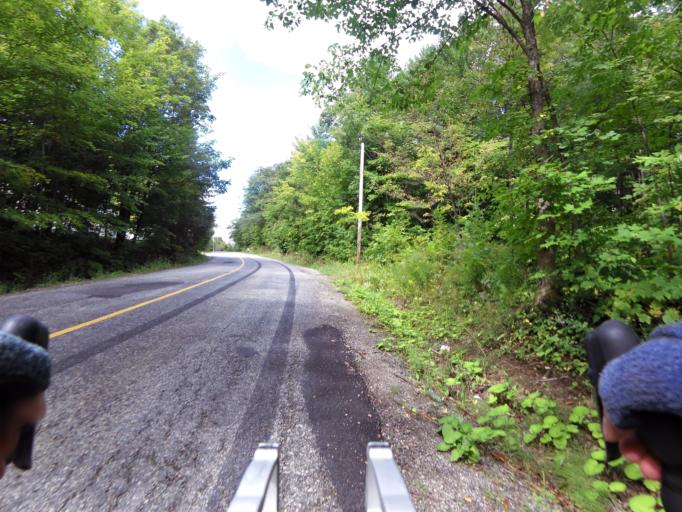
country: CA
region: Quebec
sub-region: Outaouais
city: Gatineau
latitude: 45.5648
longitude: -75.7465
